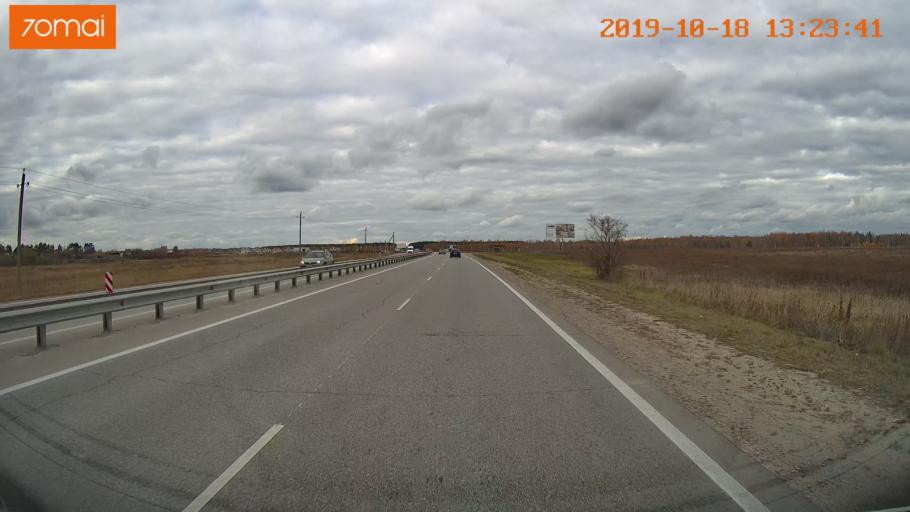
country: RU
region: Rjazan
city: Polyany
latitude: 54.7198
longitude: 39.8482
